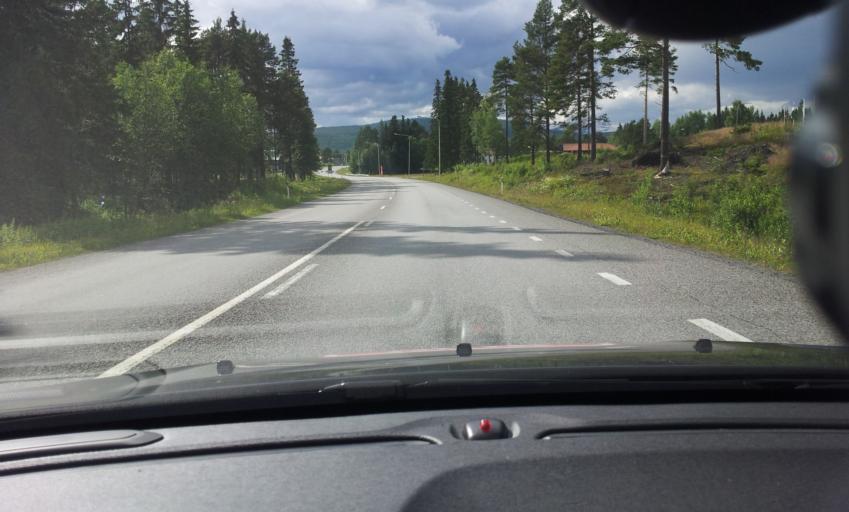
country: SE
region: Jaemtland
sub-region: Are Kommun
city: Jarpen
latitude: 63.3409
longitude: 13.4878
